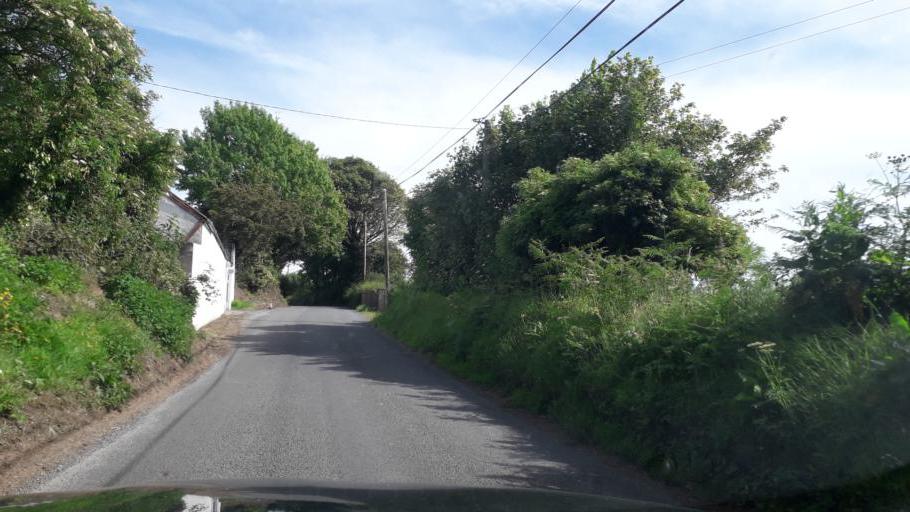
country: IE
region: Leinster
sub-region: Loch Garman
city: Castlebridge
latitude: 52.4046
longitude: -6.4054
